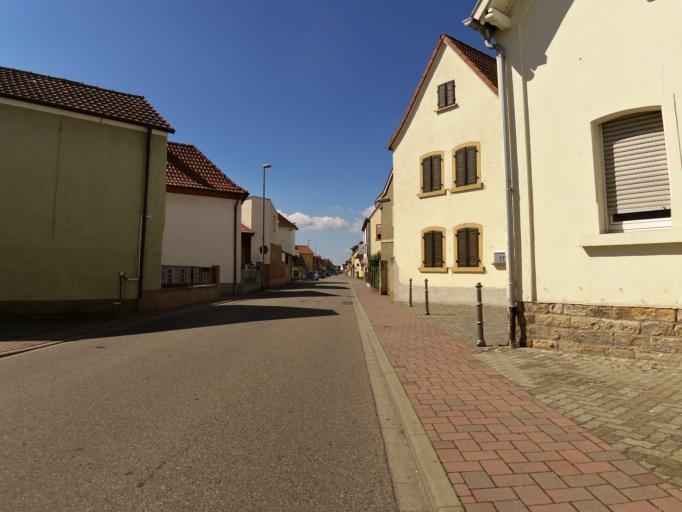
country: DE
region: Rheinland-Pfalz
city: Hassloch
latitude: 49.3586
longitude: 8.2534
